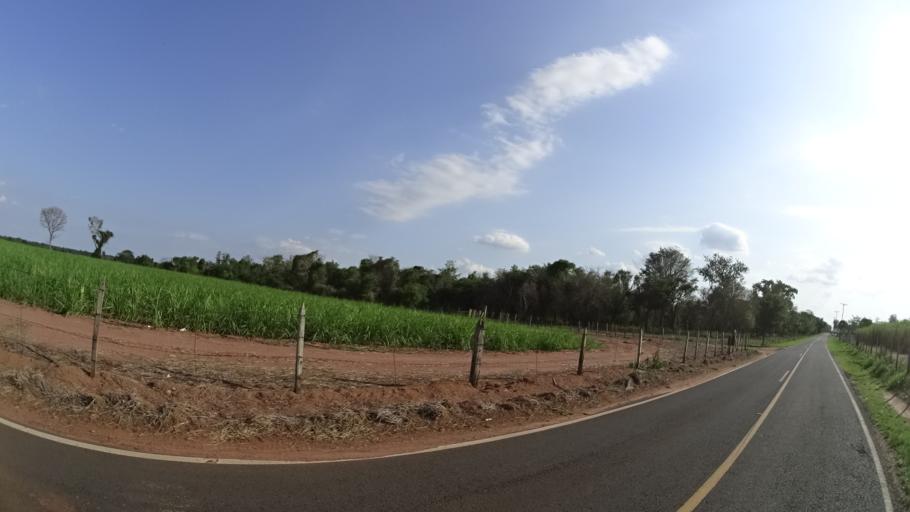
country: BR
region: Sao Paulo
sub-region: Urupes
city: Urupes
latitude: -21.3939
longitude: -49.5090
